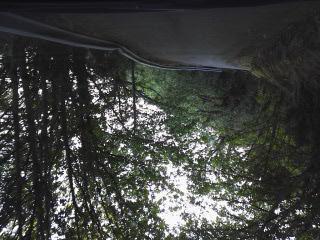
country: IT
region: Calabria
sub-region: Provincia di Vibo-Valentia
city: Nardodipace
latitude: 38.4451
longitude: 16.3391
